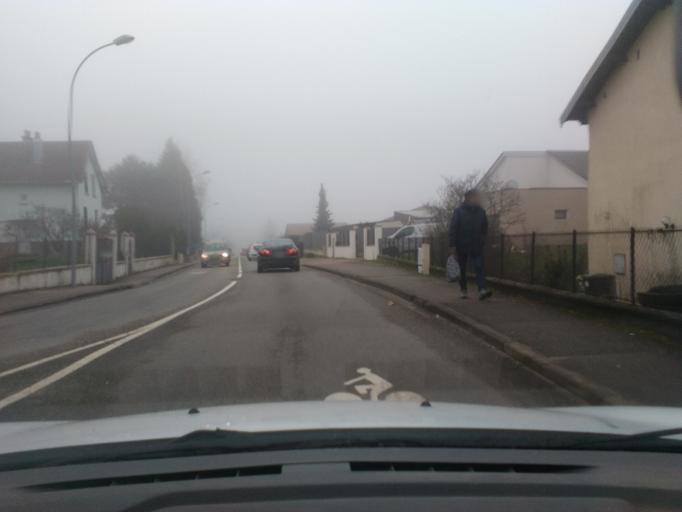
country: FR
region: Lorraine
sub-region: Departement des Vosges
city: Epinal
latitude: 48.1857
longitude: 6.4646
